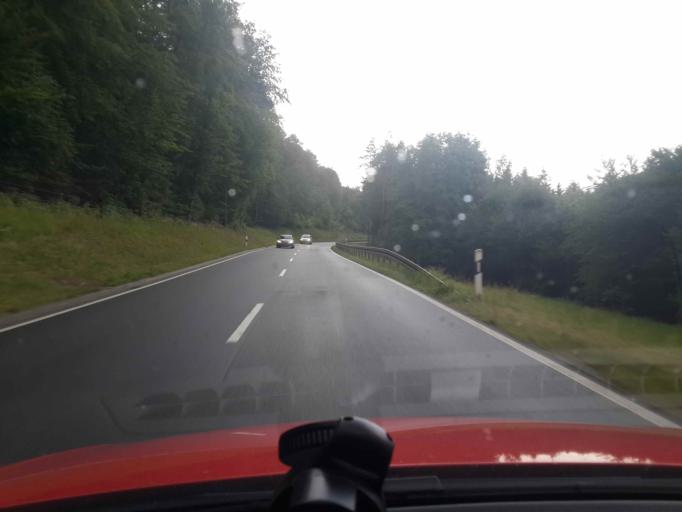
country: DE
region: Bavaria
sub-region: Regierungsbezirk Unterfranken
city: Kirchzell
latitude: 49.5992
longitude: 9.2035
